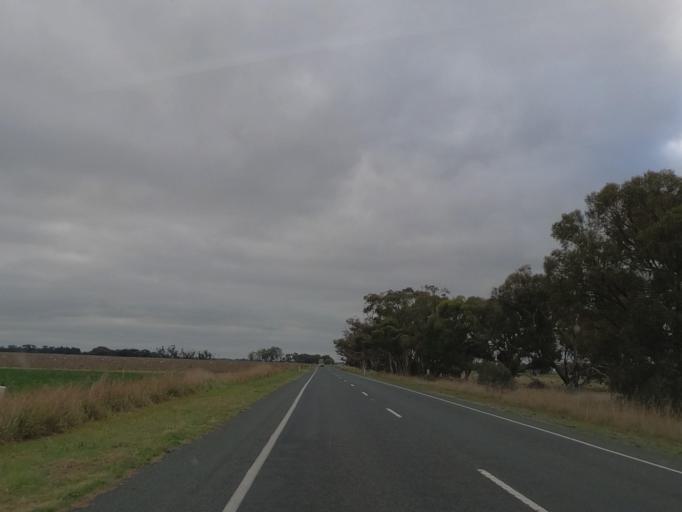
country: AU
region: Victoria
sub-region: Greater Bendigo
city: Long Gully
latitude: -36.3842
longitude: 143.9760
